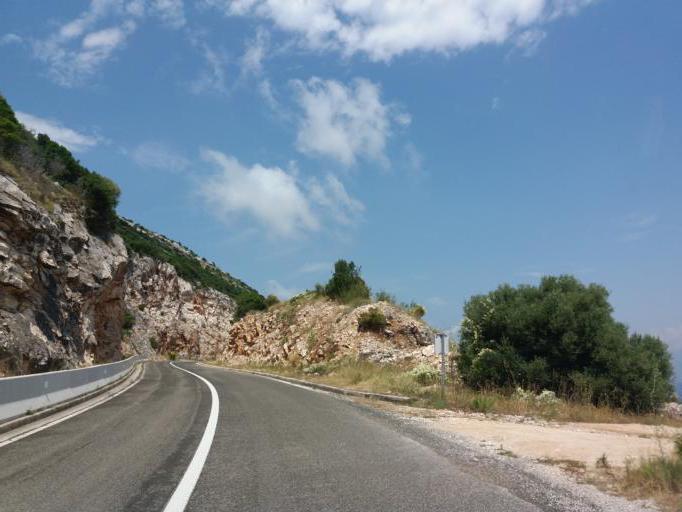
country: HR
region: Zadarska
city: Ugljan
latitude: 44.0096
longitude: 15.0469
